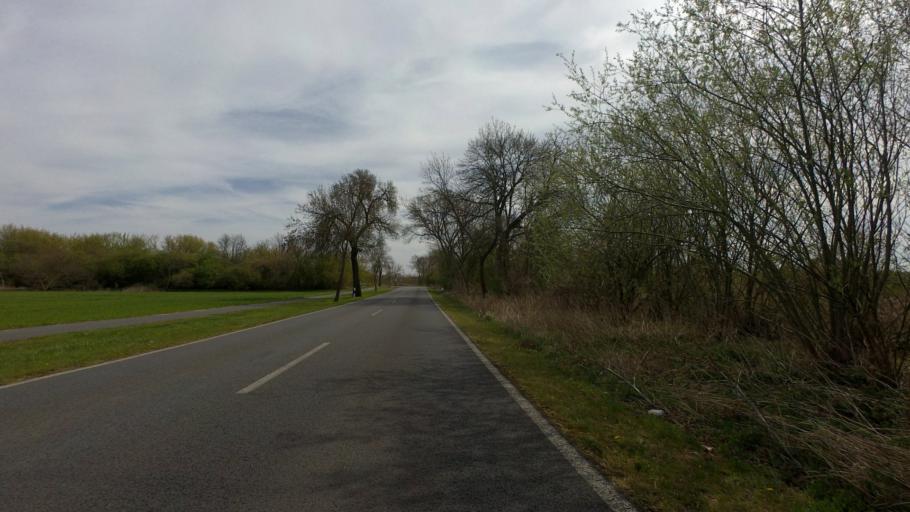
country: DE
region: Berlin
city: Gropiusstadt
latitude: 52.3765
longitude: 13.4529
